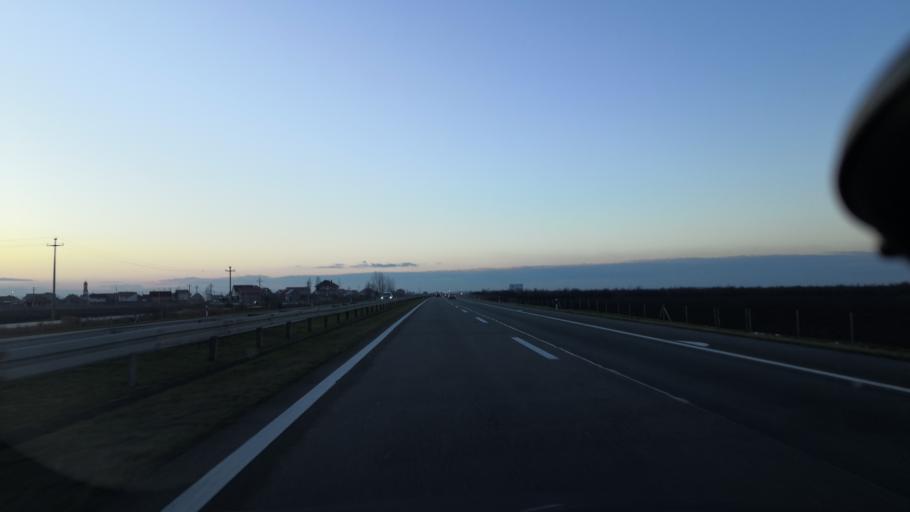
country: RS
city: Ugrinovci
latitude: 44.8550
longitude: 20.1726
